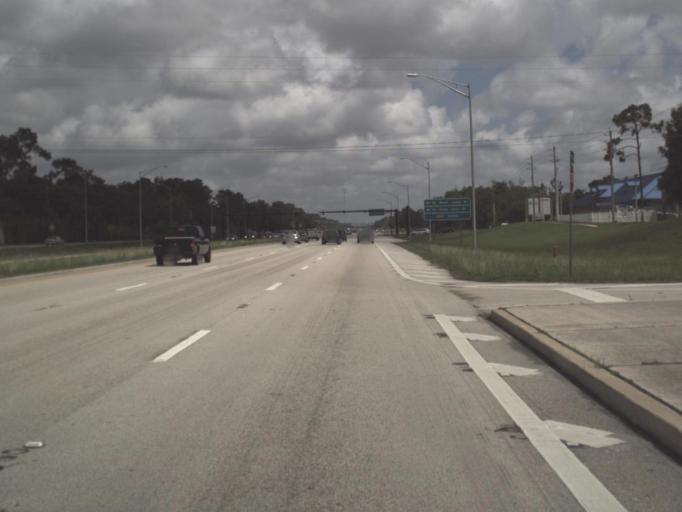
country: US
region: Florida
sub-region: Saint Johns County
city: Fruit Cove
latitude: 30.2120
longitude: -81.5517
